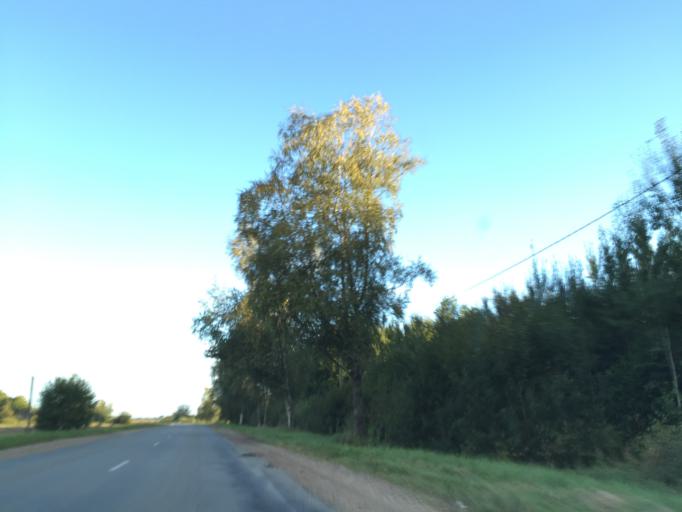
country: LV
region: Saldus Rajons
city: Saldus
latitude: 56.7303
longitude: 22.3783
